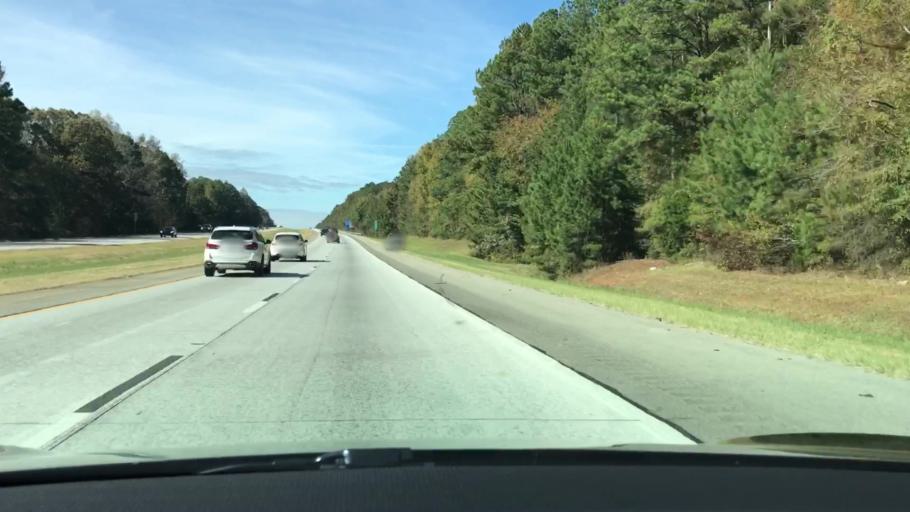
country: US
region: Georgia
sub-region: Morgan County
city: Madison
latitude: 33.5555
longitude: -83.4370
